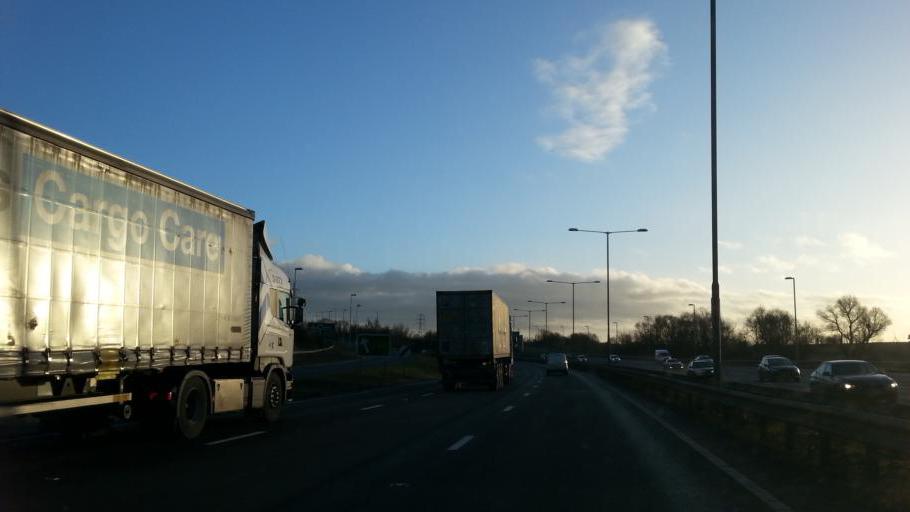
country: GB
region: England
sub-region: Northamptonshire
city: Kettering
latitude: 52.3940
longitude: -0.7500
